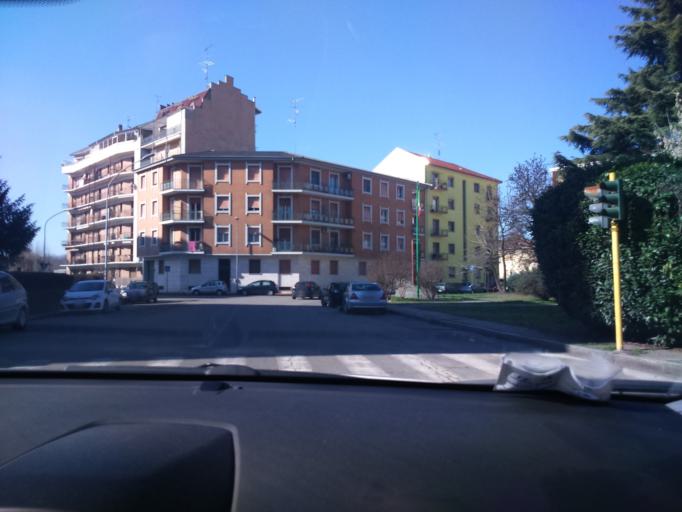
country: IT
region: Piedmont
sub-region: Provincia di Vercelli
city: Vercelli
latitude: 45.3168
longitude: 8.4189
